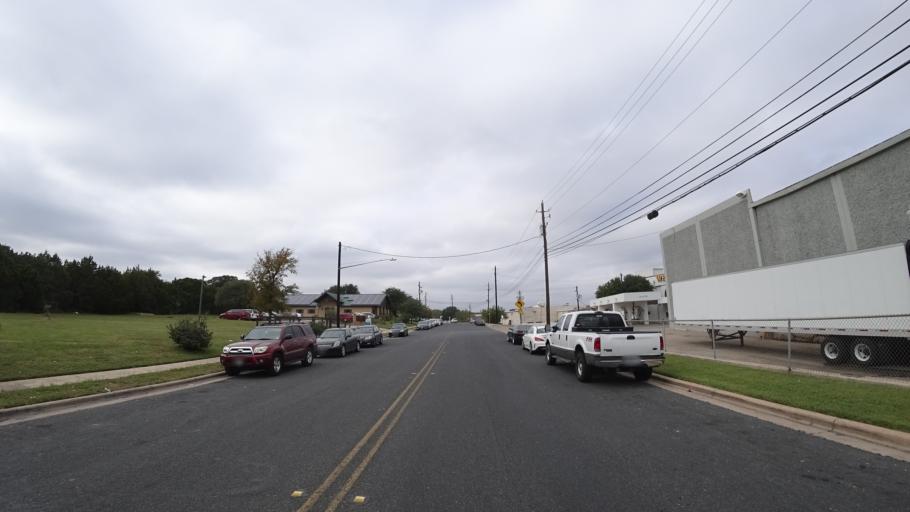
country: US
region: Texas
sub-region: Travis County
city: Barton Creek
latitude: 30.2330
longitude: -97.8769
